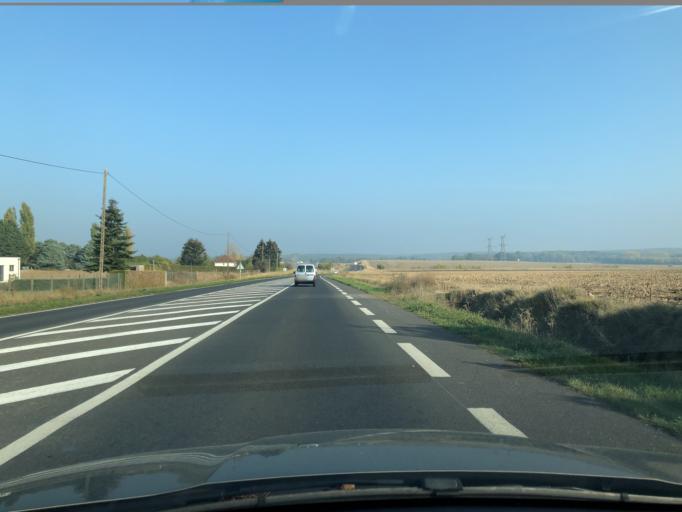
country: FR
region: Centre
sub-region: Departement d'Indre-et-Loire
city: Chanceaux-sur-Choisille
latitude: 47.4738
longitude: 0.6949
